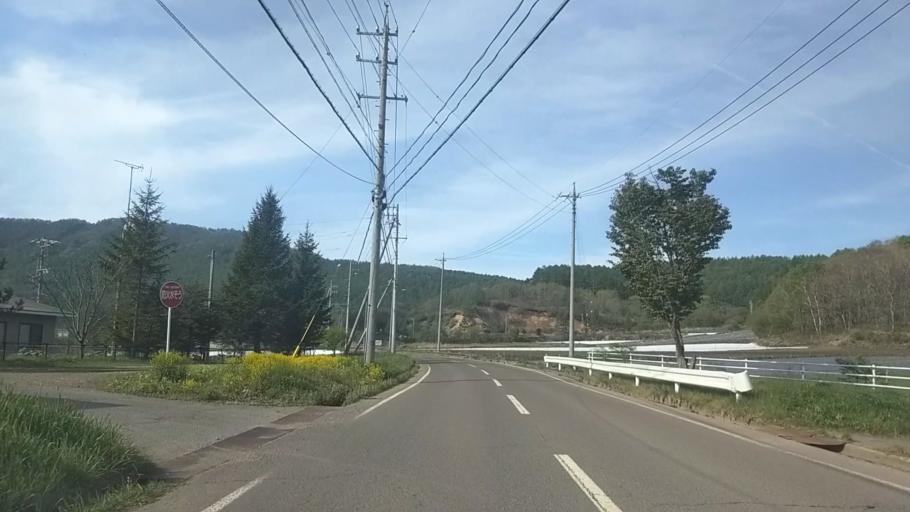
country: JP
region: Yamanashi
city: Nirasaki
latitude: 35.9402
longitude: 138.4665
